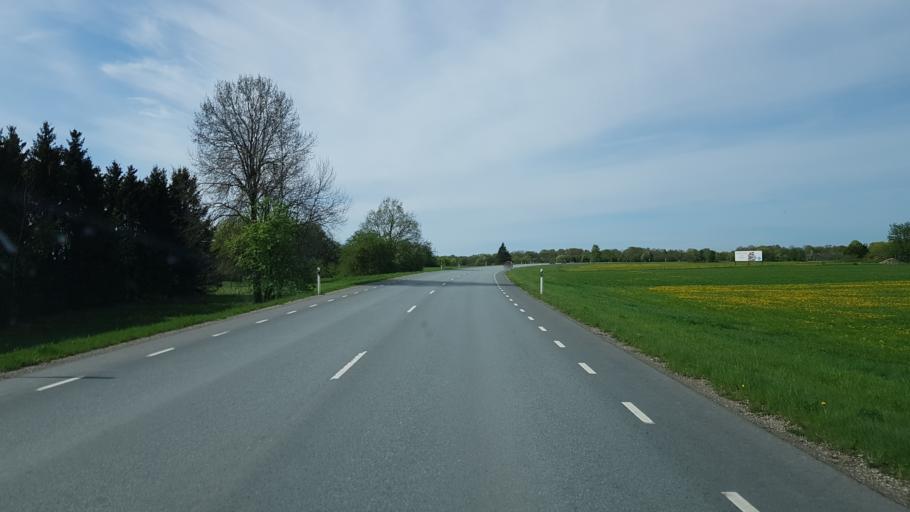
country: EE
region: Saare
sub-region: Kuressaare linn
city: Kuressaare
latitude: 58.2984
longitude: 22.5748
